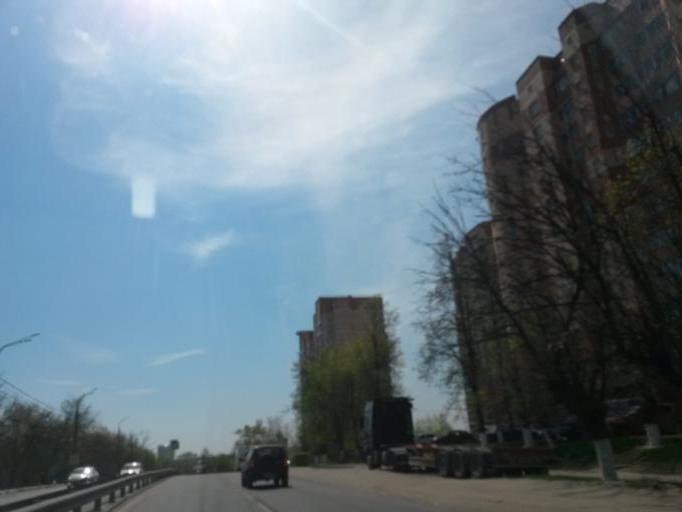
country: RU
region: Moskovskaya
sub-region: Podol'skiy Rayon
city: Podol'sk
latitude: 55.4469
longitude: 37.5520
